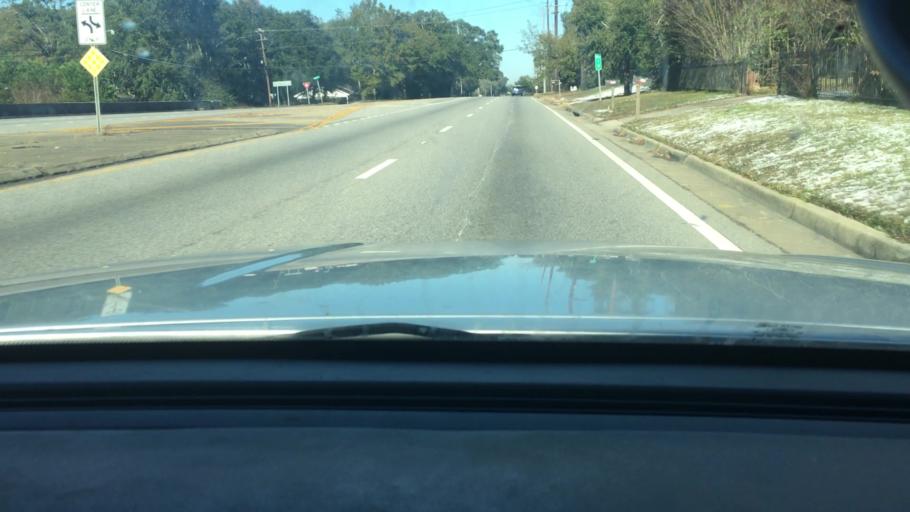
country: US
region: Alabama
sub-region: Mobile County
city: Prichard
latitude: 30.7222
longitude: -88.1652
